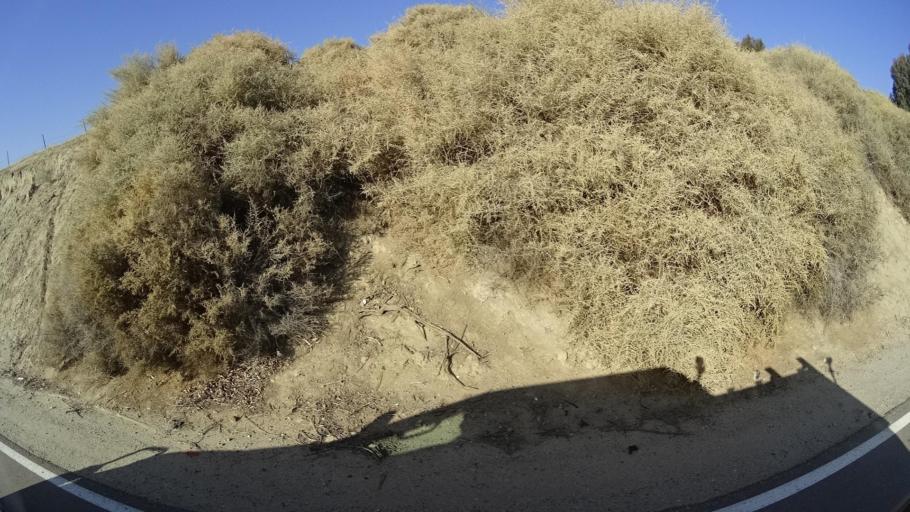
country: US
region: California
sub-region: Kern County
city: Oildale
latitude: 35.4513
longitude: -118.9151
